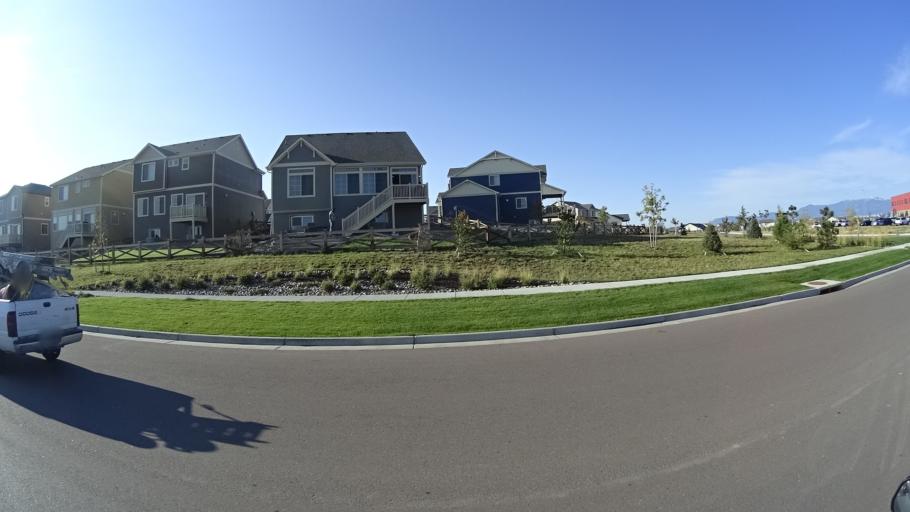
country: US
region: Colorado
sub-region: El Paso County
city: Cimarron Hills
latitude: 38.9317
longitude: -104.6571
